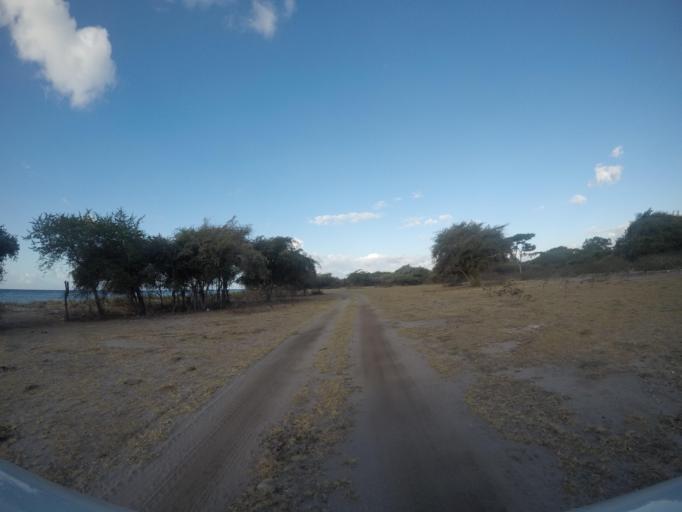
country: TL
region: Lautem
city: Lospalos
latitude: -8.3239
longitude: 126.9950
